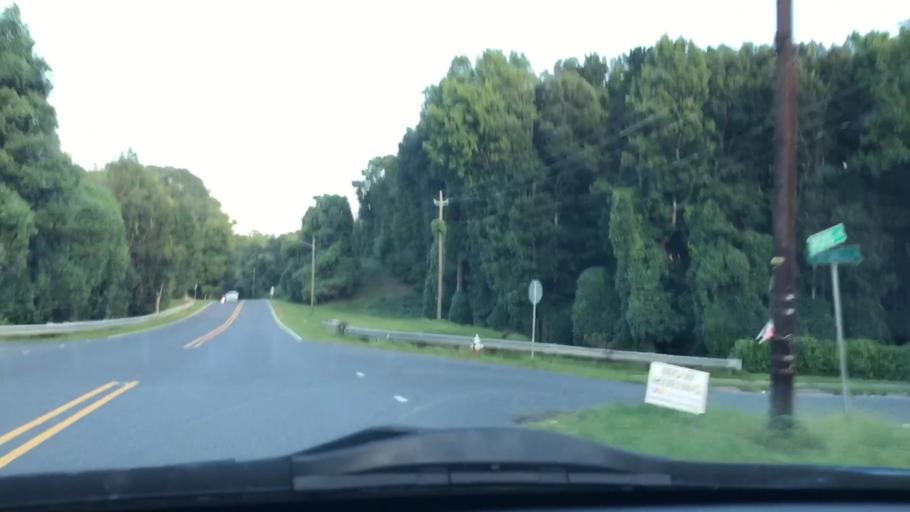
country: US
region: North Carolina
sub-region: Randolph County
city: Asheboro
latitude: 35.7152
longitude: -79.8191
